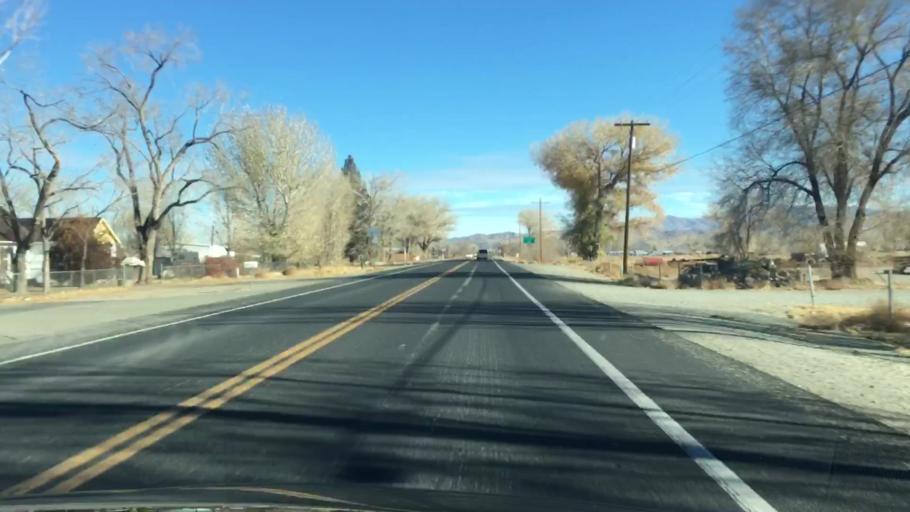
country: US
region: Nevada
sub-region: Lyon County
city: Yerington
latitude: 38.9974
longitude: -119.1579
